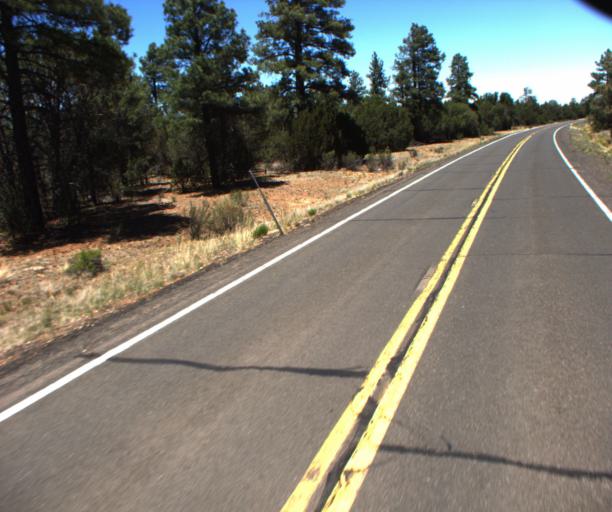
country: US
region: Arizona
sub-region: Gila County
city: Star Valley
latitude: 34.6835
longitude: -111.1127
